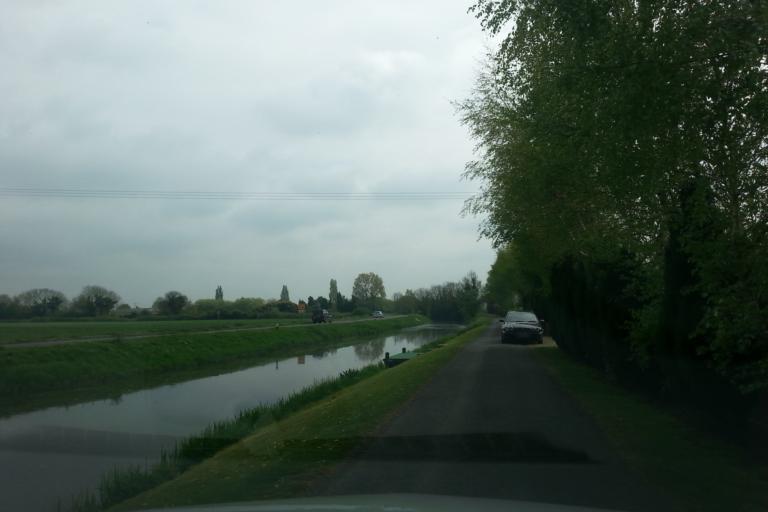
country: GB
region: England
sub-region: Norfolk
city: Outwell
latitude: 52.6073
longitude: 0.2479
